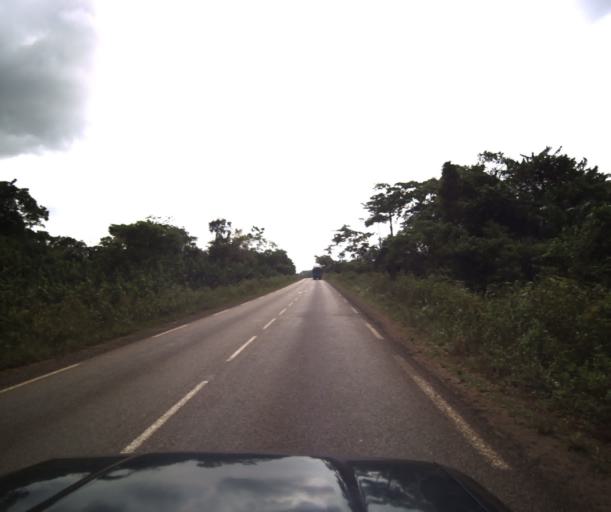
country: CM
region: Littoral
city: Edea
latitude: 3.8158
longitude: 10.3470
